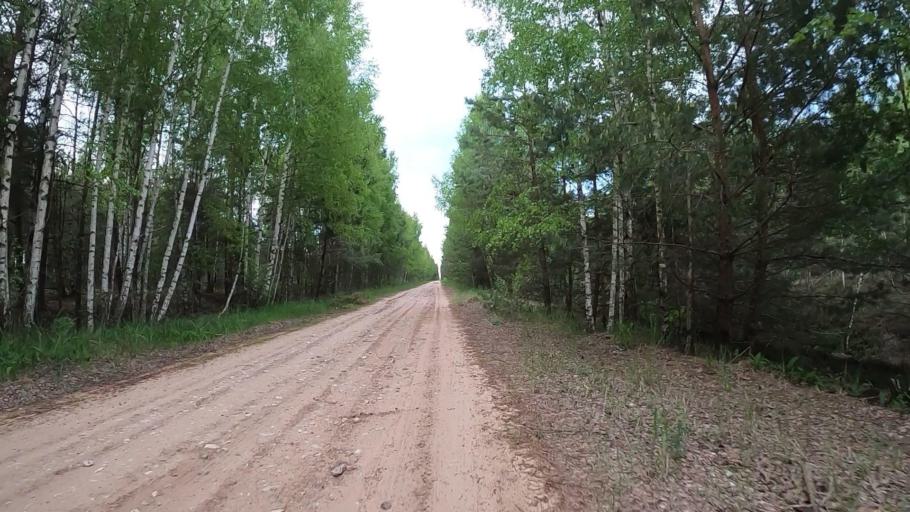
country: LV
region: Olaine
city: Olaine
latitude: 56.8436
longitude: 23.9342
